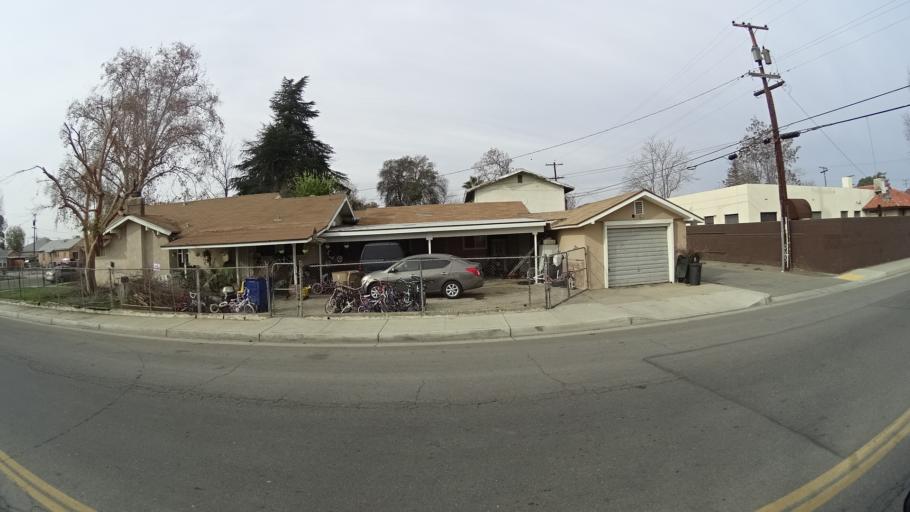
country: US
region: California
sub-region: Kern County
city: Bakersfield
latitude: 35.3602
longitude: -119.0165
